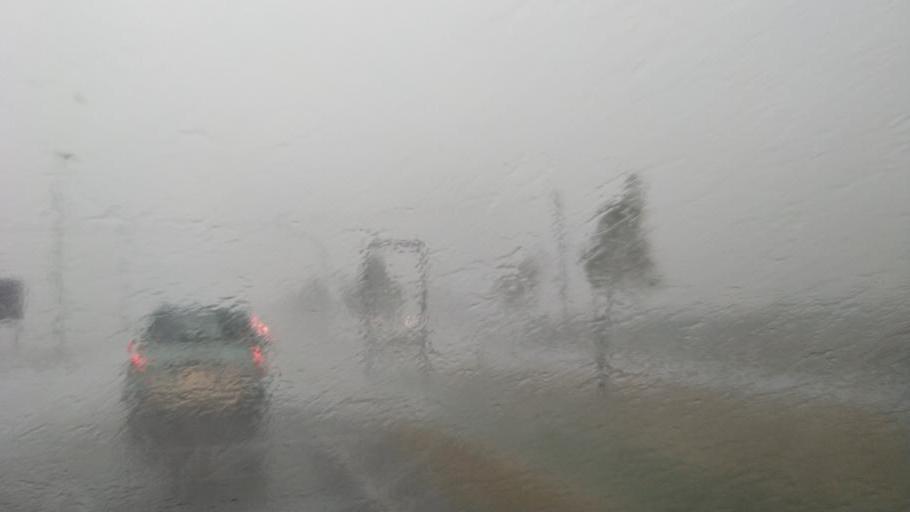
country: IT
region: Emilia-Romagna
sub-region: Provincia di Ferrara
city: Pontegradella
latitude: 44.8472
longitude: 11.6459
